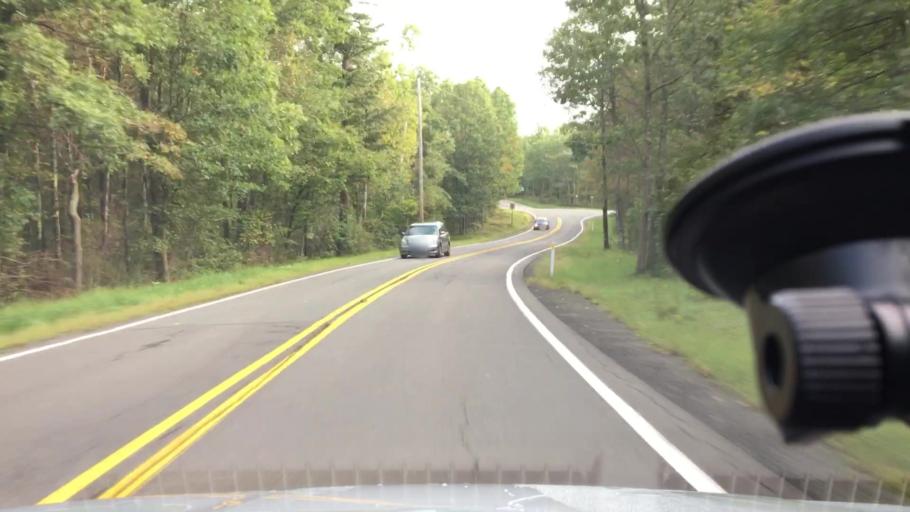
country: US
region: Pennsylvania
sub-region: Monroe County
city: Mountainhome
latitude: 41.1382
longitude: -75.2613
